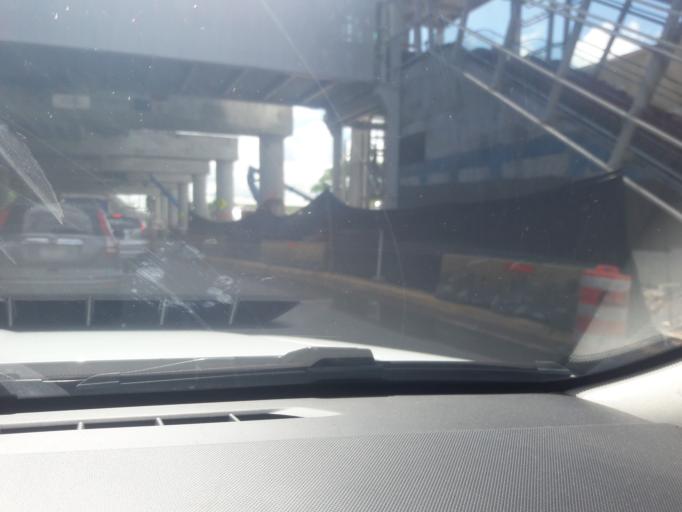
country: PA
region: Panama
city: San Miguelito
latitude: 9.0522
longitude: -79.4443
